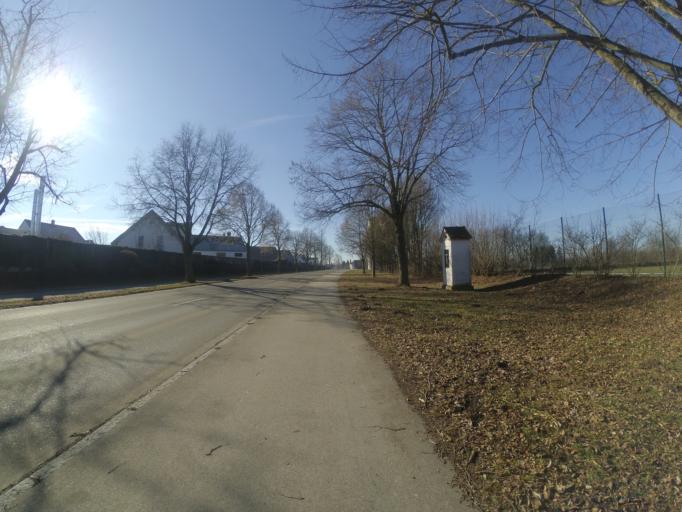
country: DE
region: Baden-Wuerttemberg
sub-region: Tuebingen Region
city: Erbach
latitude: 48.3335
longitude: 9.9345
